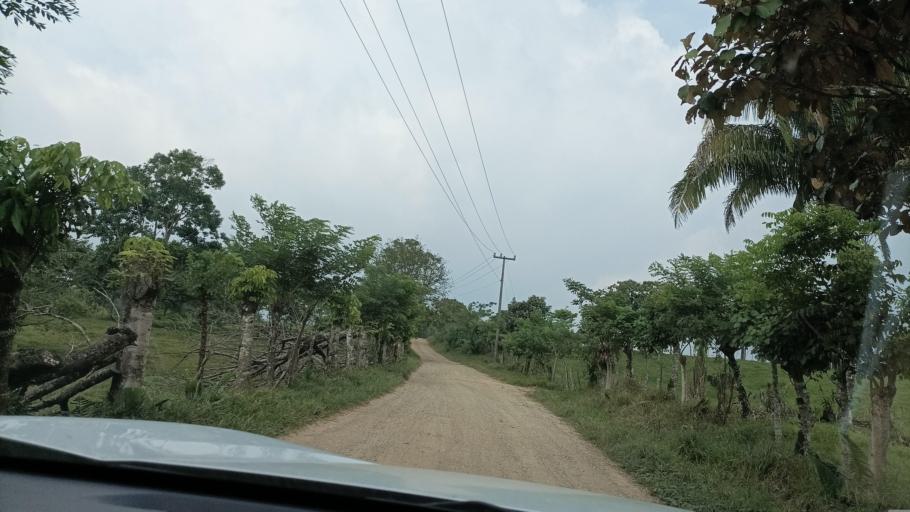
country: MX
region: Tabasco
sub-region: Huimanguillo
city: Francisco Rueda
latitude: 17.5898
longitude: -94.1995
